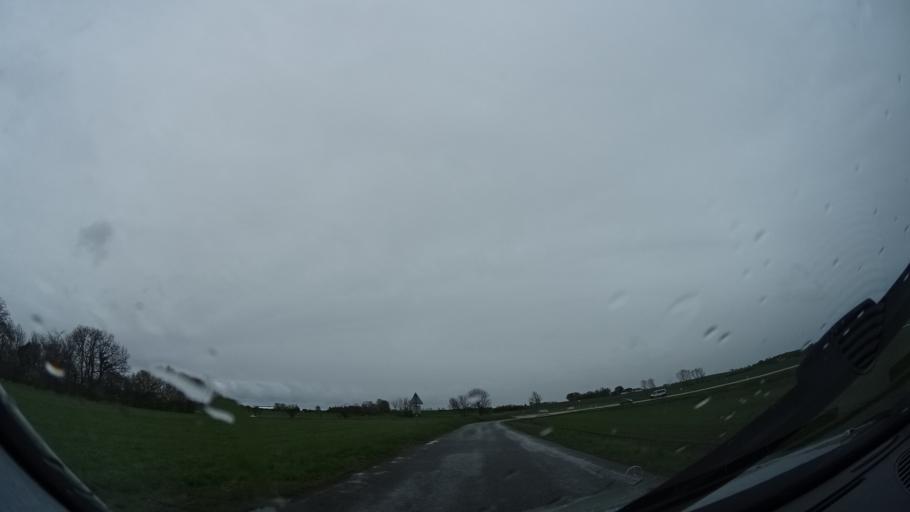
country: DK
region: Zealand
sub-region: Lejre Kommune
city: Ejby
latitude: 55.6975
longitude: 11.8740
